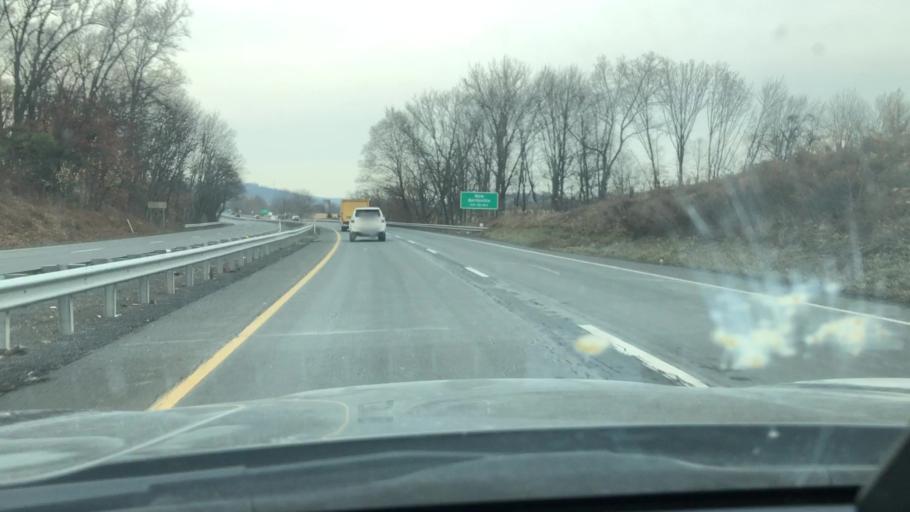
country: US
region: Pennsylvania
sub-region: Berks County
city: New Berlinville
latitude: 40.3412
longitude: -75.6221
